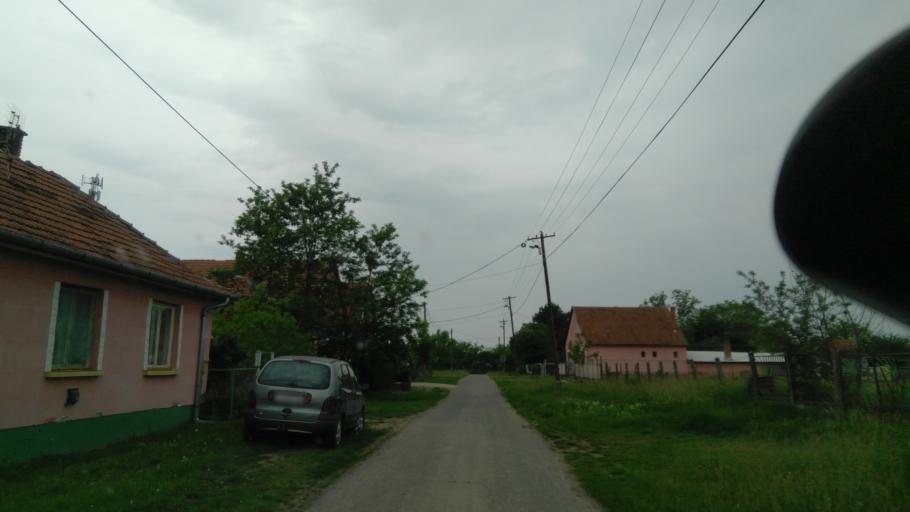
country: HU
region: Bekes
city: Doboz
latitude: 46.7256
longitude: 21.2481
